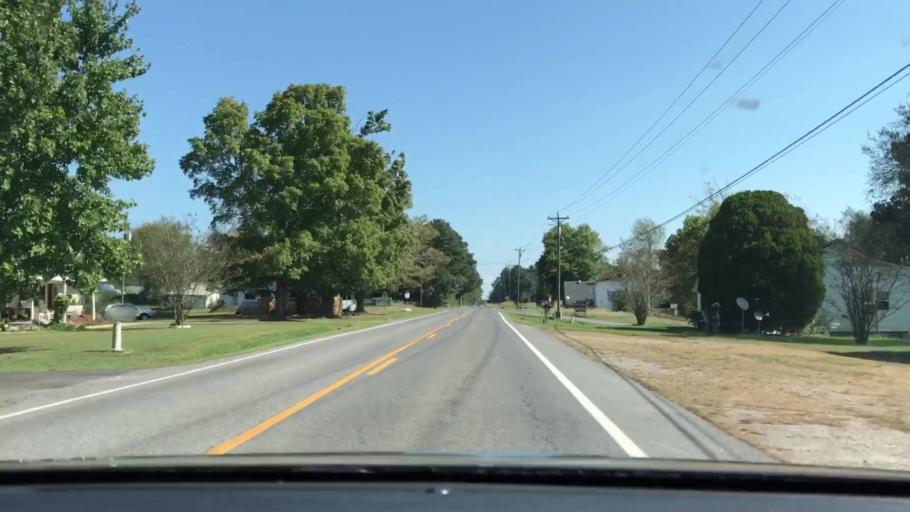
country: US
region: Kentucky
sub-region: Marshall County
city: Benton
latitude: 36.7700
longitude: -88.1742
